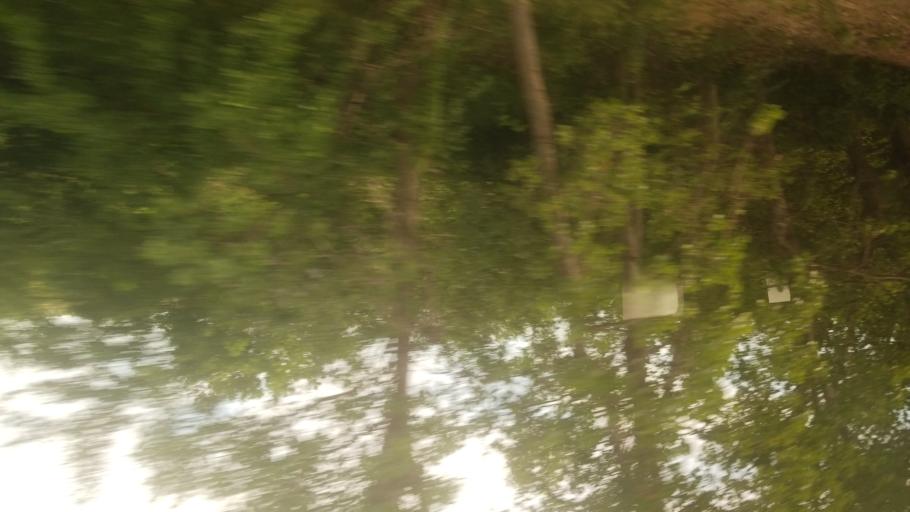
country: US
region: Kansas
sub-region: Douglas County
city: Lawrence
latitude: 38.9538
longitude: -95.1933
